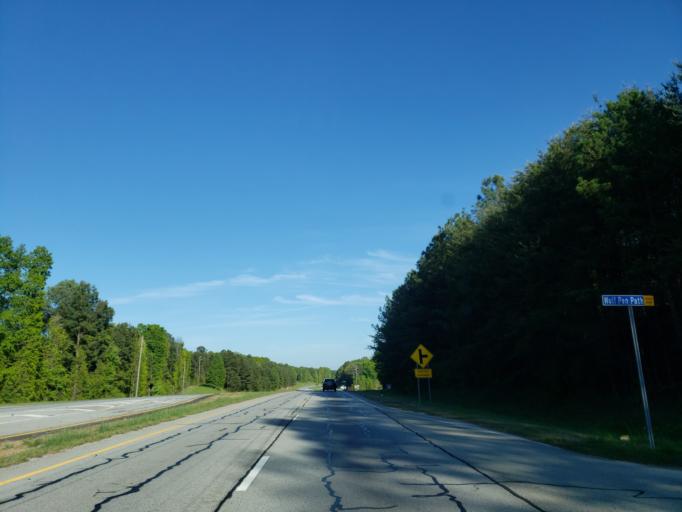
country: US
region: Georgia
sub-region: Paulding County
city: Dallas
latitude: 33.9257
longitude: -84.9426
